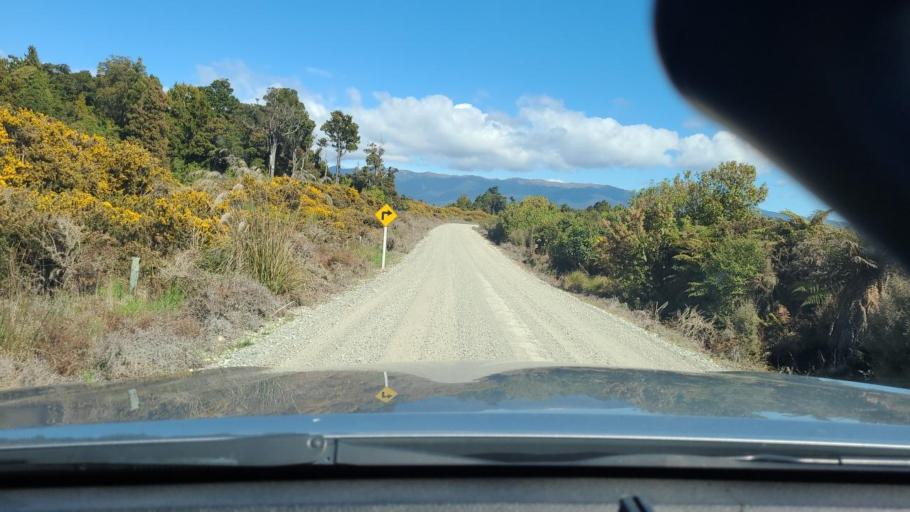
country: NZ
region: Southland
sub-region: Southland District
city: Riverton
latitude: -46.1449
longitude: 167.4902
